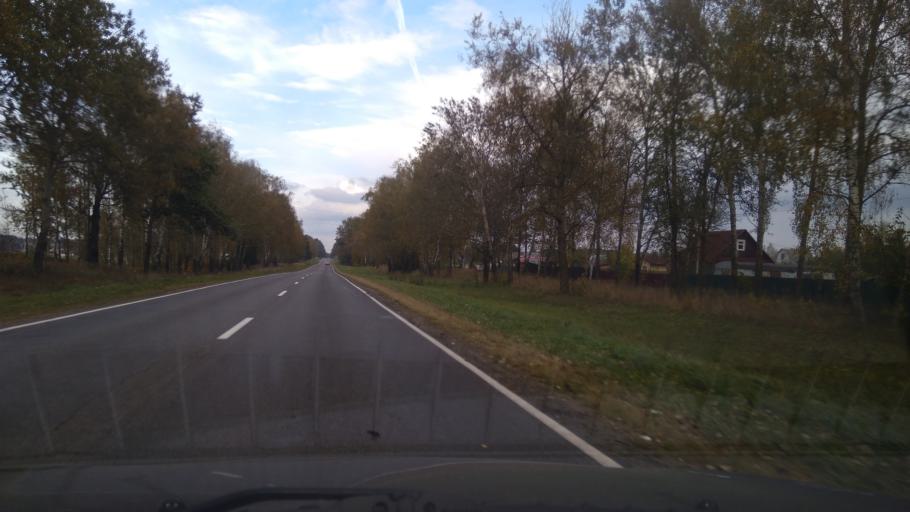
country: BY
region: Minsk
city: Rudzyensk
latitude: 53.6208
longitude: 27.8597
